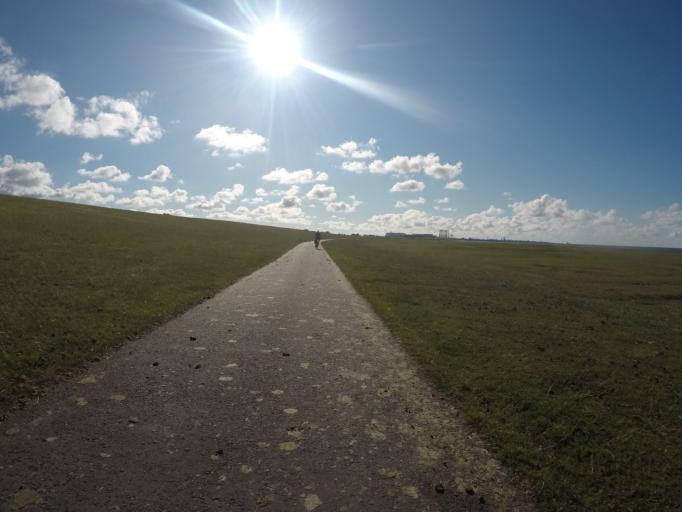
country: DE
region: Lower Saxony
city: Nordleda
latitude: 53.8324
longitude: 8.7937
